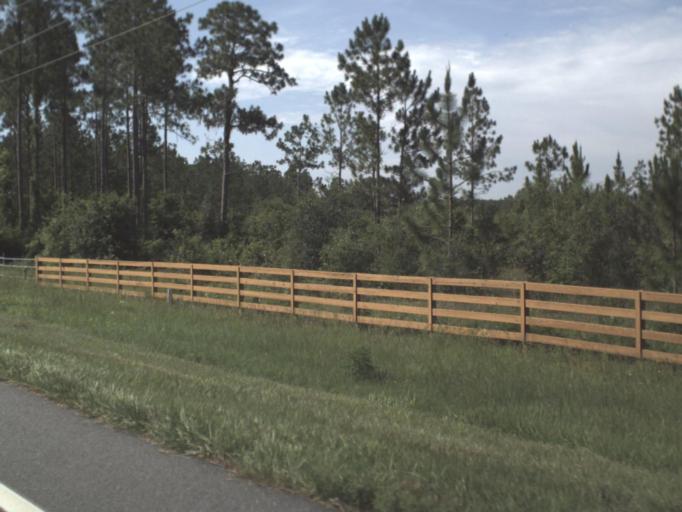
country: US
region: Florida
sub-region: Madison County
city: Madison
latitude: 30.4186
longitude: -83.3762
